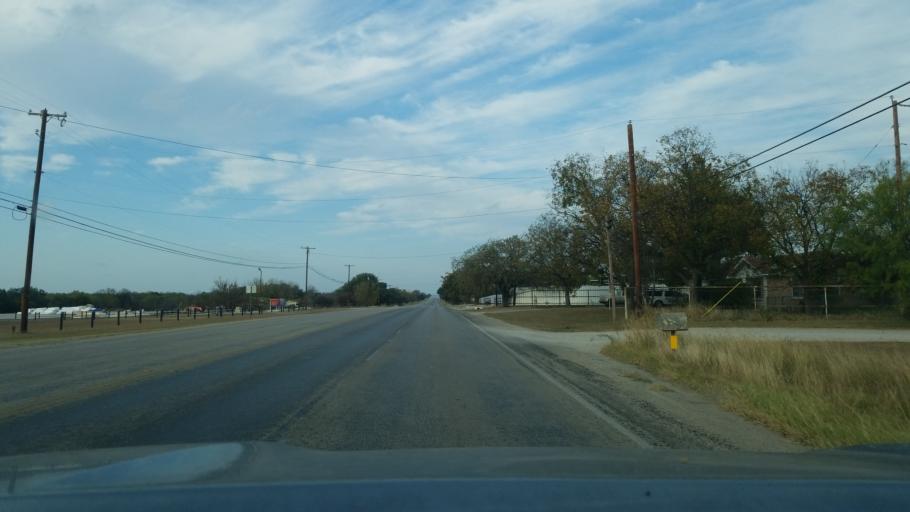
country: US
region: Texas
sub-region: Brown County
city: Early
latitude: 31.7572
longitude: -98.9594
